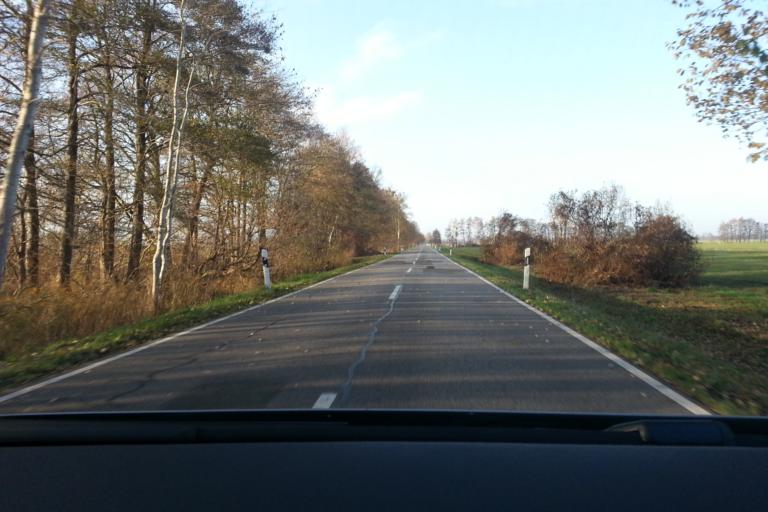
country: DE
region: Mecklenburg-Vorpommern
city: Strasburg
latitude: 53.6384
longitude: 13.7471
